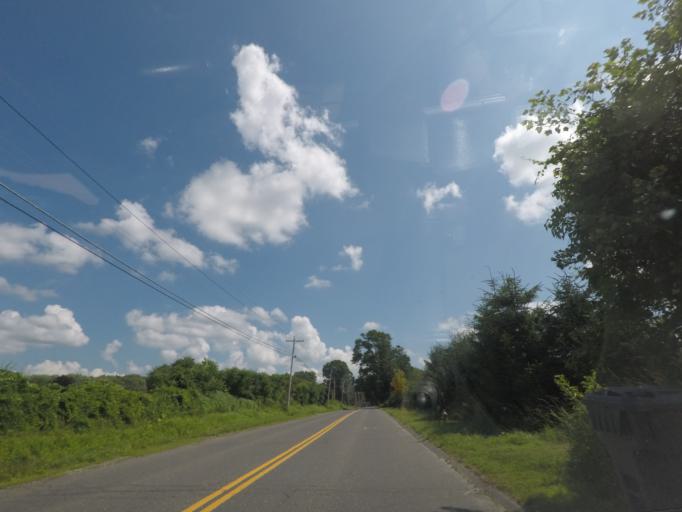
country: US
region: Massachusetts
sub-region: Hampden County
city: Monson
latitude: 42.1259
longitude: -72.3335
